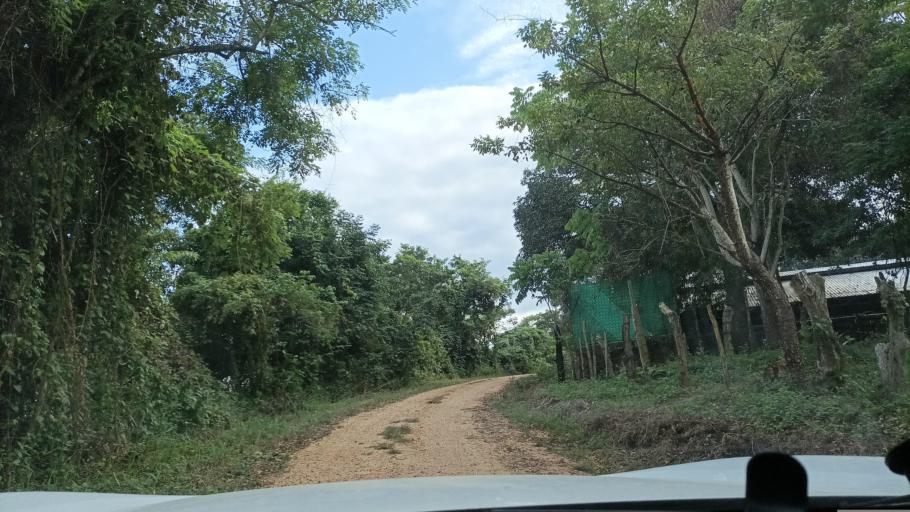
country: MX
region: Veracruz
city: Oluta
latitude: 17.9431
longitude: -94.8821
